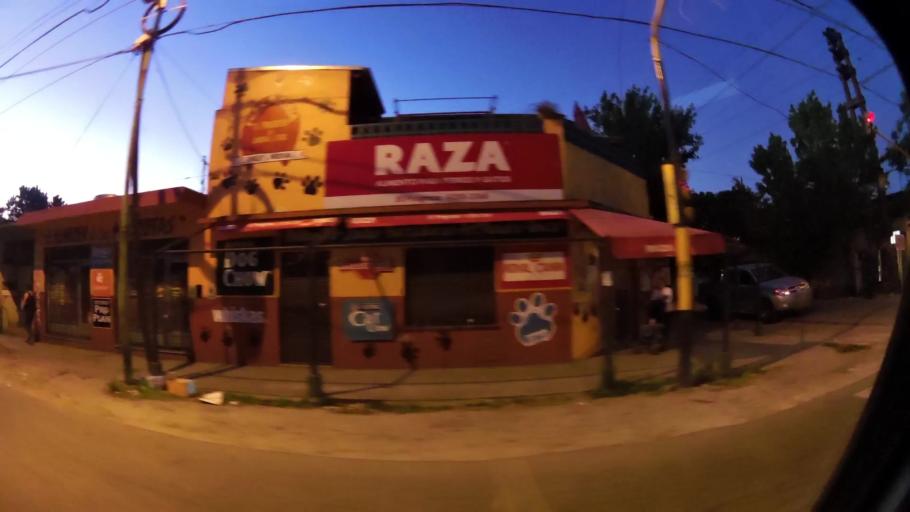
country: AR
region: Buenos Aires
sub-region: Partido de Quilmes
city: Quilmes
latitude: -34.7798
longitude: -58.1793
